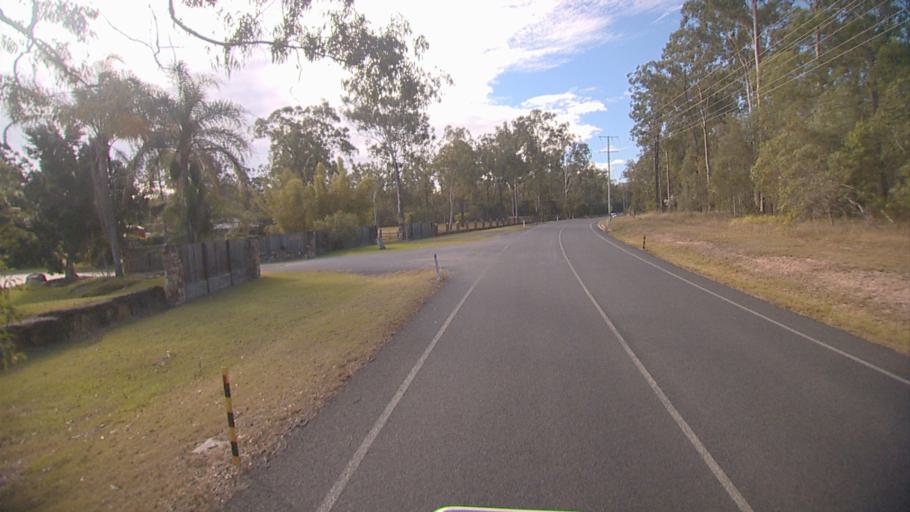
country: AU
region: Queensland
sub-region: Logan
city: North Maclean
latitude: -27.8122
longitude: 153.0567
